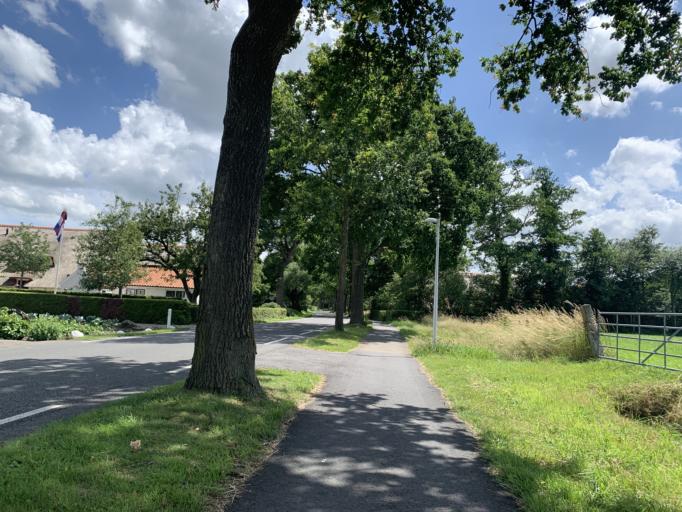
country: NL
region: Groningen
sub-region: Gemeente Haren
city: Haren
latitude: 53.1471
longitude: 6.6479
